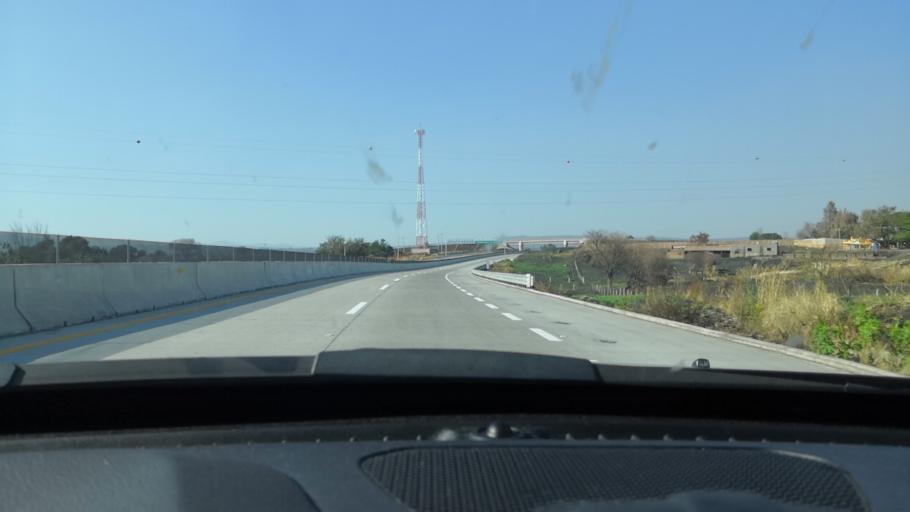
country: MX
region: Jalisco
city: Zapotlanejo
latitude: 20.6033
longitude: -103.1022
